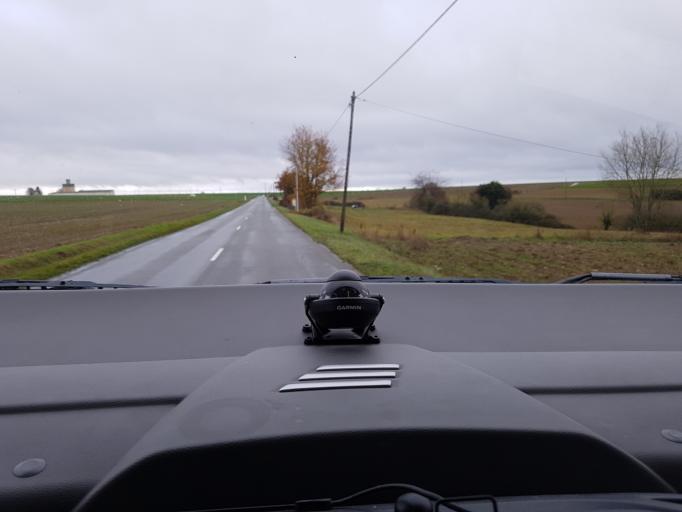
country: FR
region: Haute-Normandie
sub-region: Departement de l'Eure
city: Pont-Saint-Pierre
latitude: 49.3075
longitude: 1.3155
